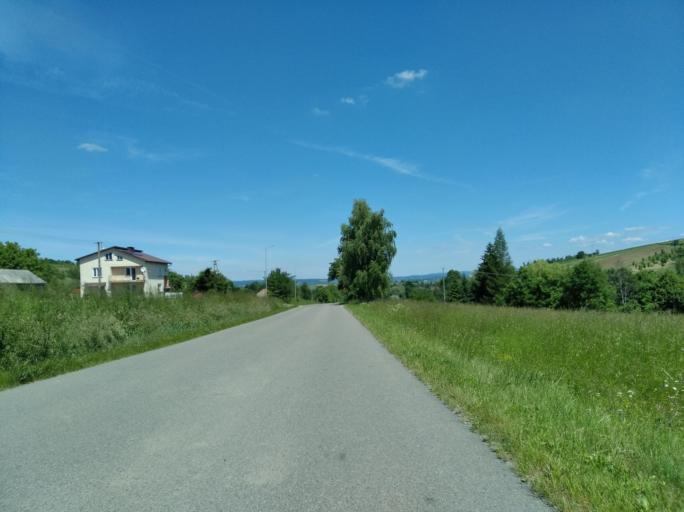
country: PL
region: Subcarpathian Voivodeship
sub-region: Powiat jasielski
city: Tarnowiec
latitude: 49.6825
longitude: 21.5438
